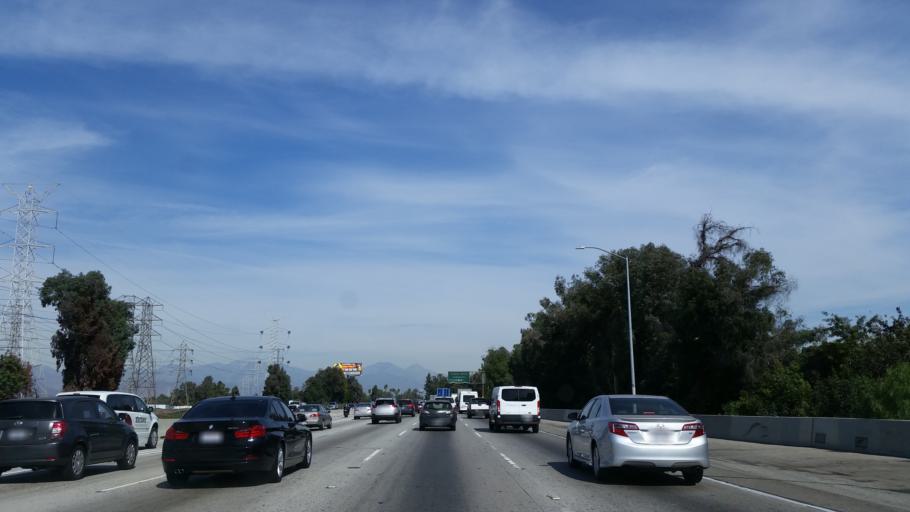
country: US
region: California
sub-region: Los Angeles County
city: Avocado Heights
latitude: 34.0398
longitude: -118.0177
